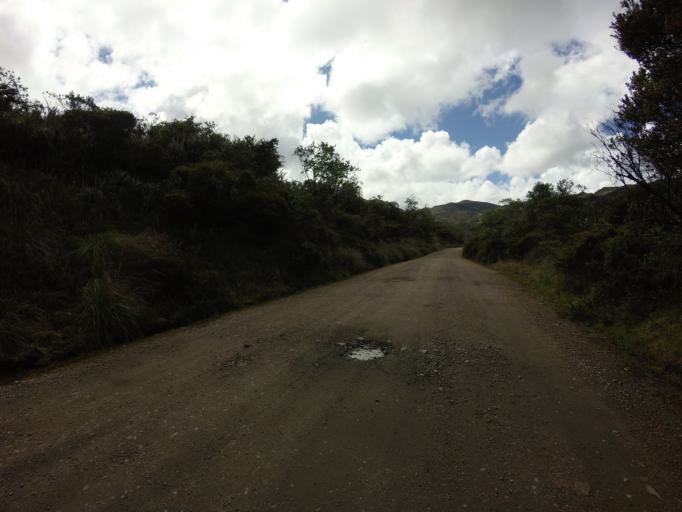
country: CO
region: Cundinamarca
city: Junin
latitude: 4.6254
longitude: -73.7229
